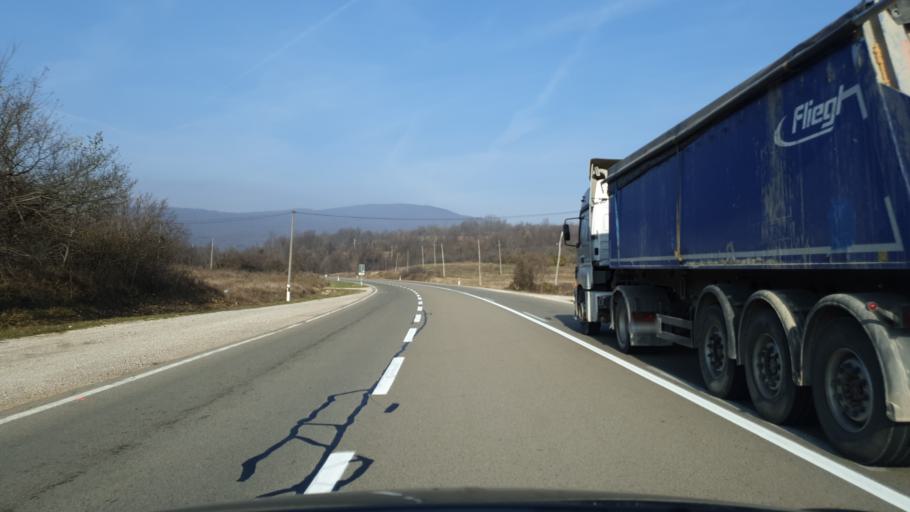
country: RS
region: Central Serbia
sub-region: Nisavski Okrug
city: Razanj
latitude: 43.8372
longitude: 21.7163
